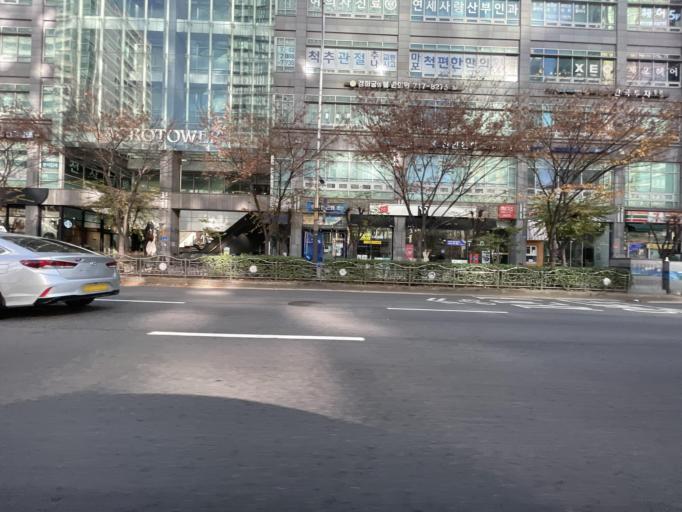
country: KR
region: Seoul
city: Seoul
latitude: 37.5414
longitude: 126.9487
